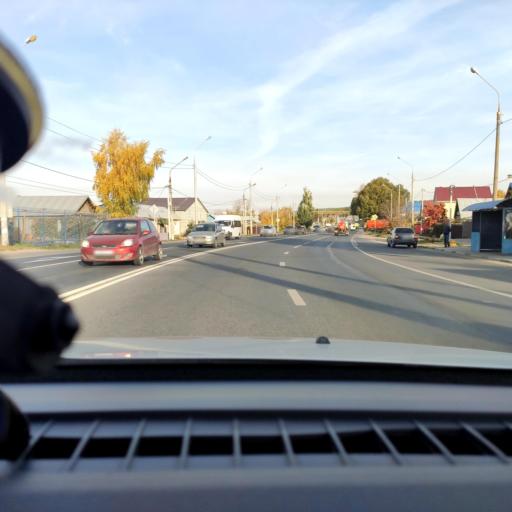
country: RU
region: Samara
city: Volzhskiy
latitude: 53.4266
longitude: 50.1211
